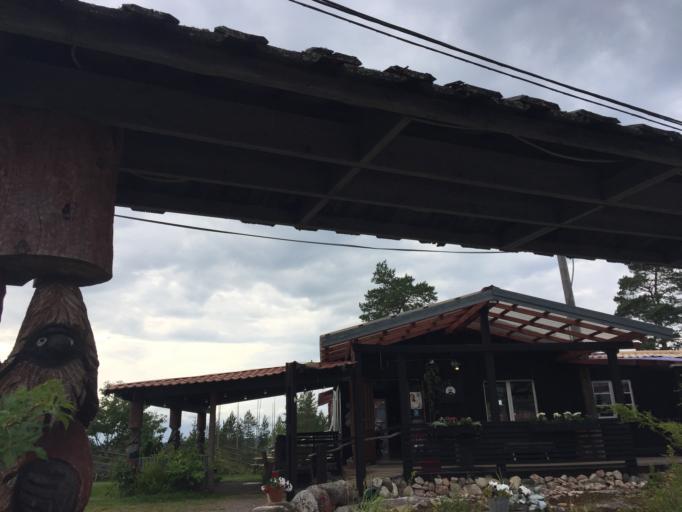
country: SE
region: Vaermland
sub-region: Filipstads Kommun
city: Filipstad
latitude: 59.7314
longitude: 14.1984
